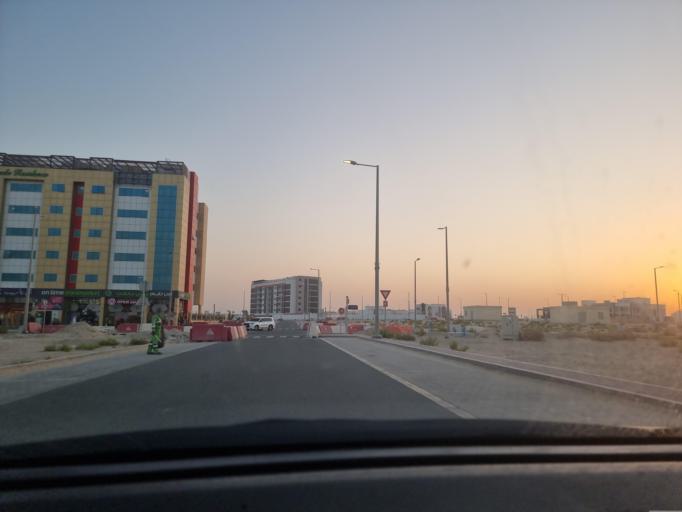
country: AE
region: Abu Dhabi
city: Abu Dhabi
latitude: 24.3692
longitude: 54.7403
